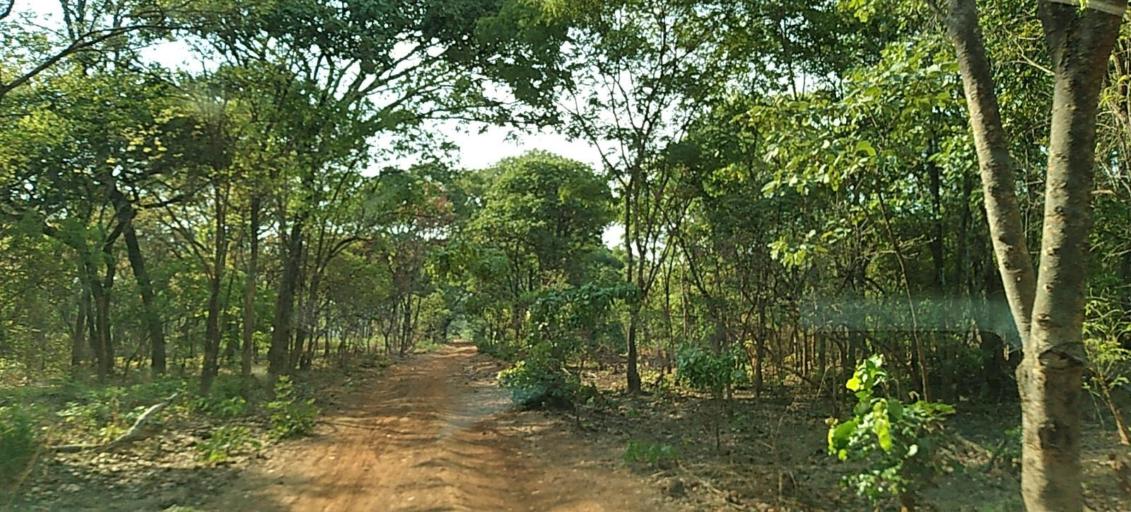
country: ZM
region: Copperbelt
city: Kalulushi
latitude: -13.0040
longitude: 27.7152
